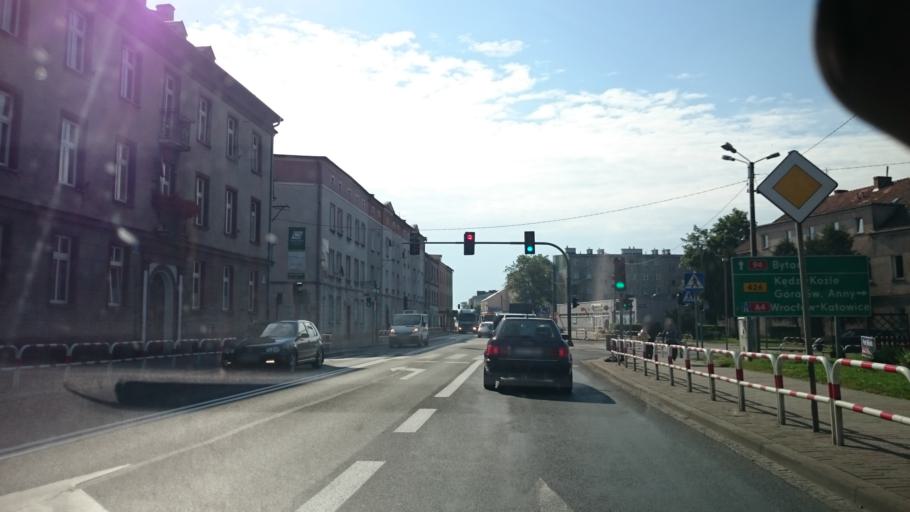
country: PL
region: Opole Voivodeship
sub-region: Powiat strzelecki
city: Strzelce Opolskie
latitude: 50.5100
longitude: 18.3020
